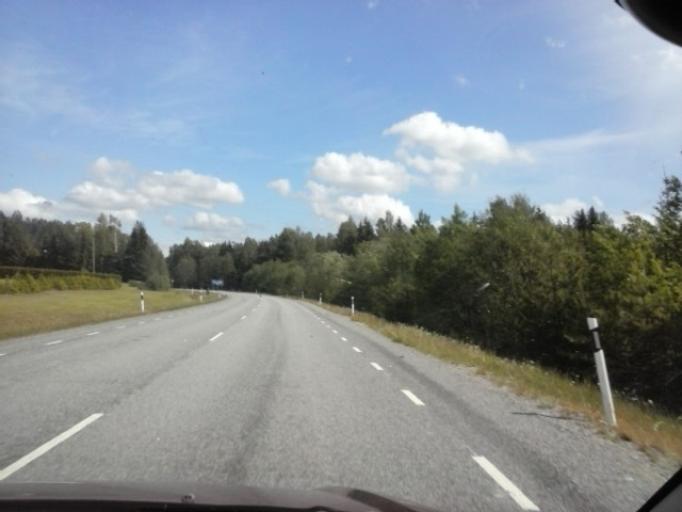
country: EE
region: Raplamaa
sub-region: Rapla vald
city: Rapla
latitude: 58.9911
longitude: 24.7766
